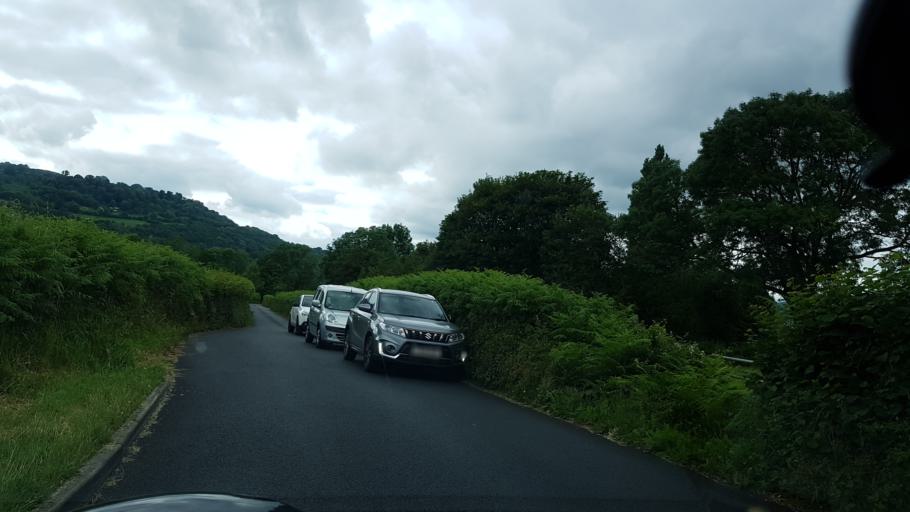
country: GB
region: Wales
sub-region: Monmouthshire
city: Gilwern
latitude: 51.8335
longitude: -3.0960
